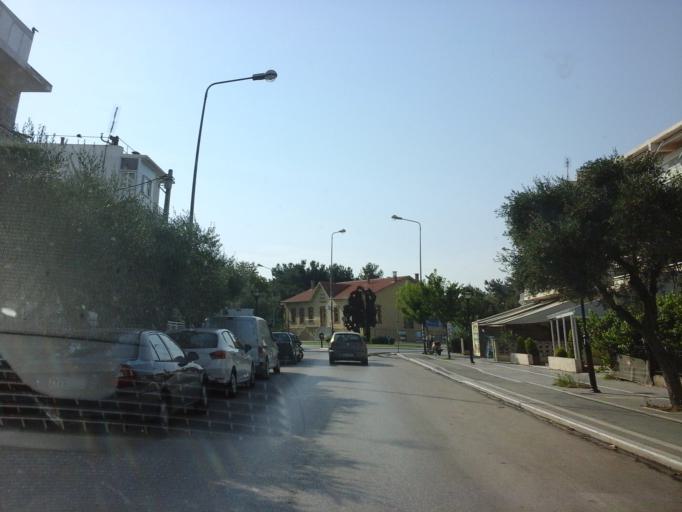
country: GR
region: East Macedonia and Thrace
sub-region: Nomos Evrou
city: Alexandroupoli
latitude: 40.8525
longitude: 25.8707
